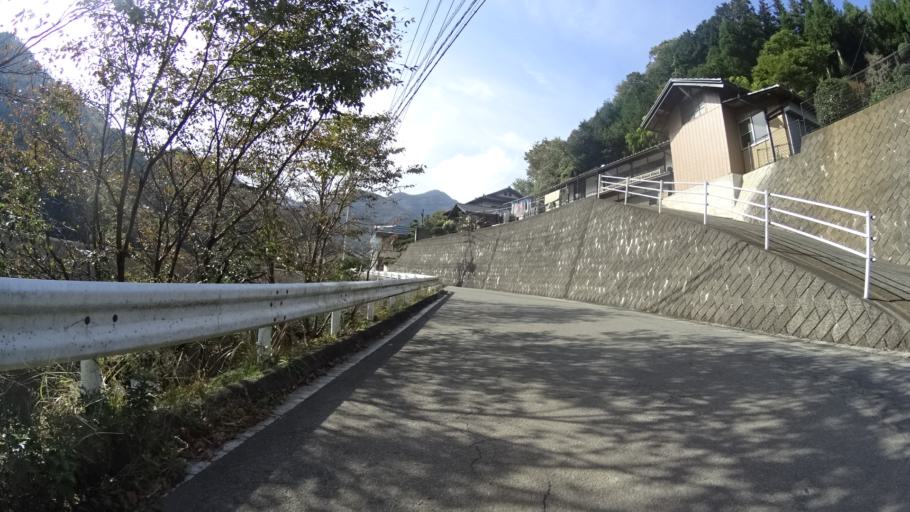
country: JP
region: Yamanashi
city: Otsuki
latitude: 35.5950
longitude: 138.9692
